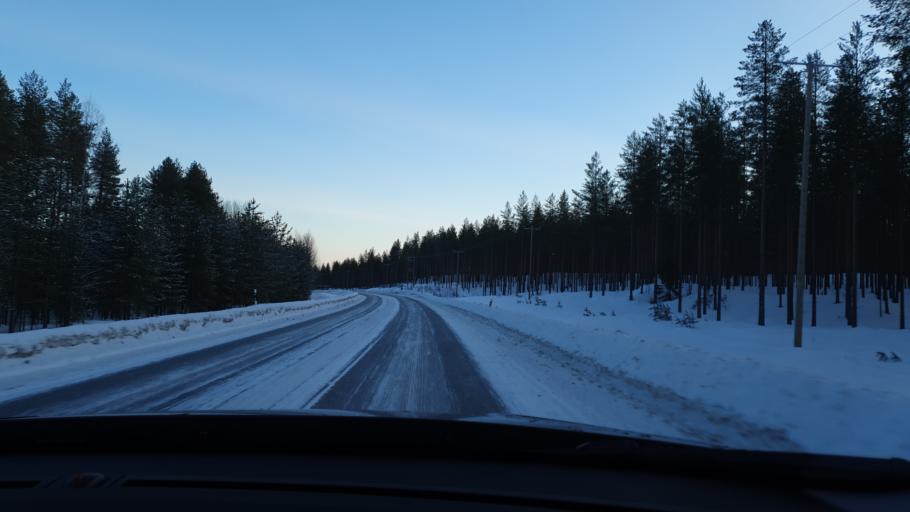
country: FI
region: Kainuu
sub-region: Kajaani
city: Sotkamo
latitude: 64.0926
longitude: 28.5536
